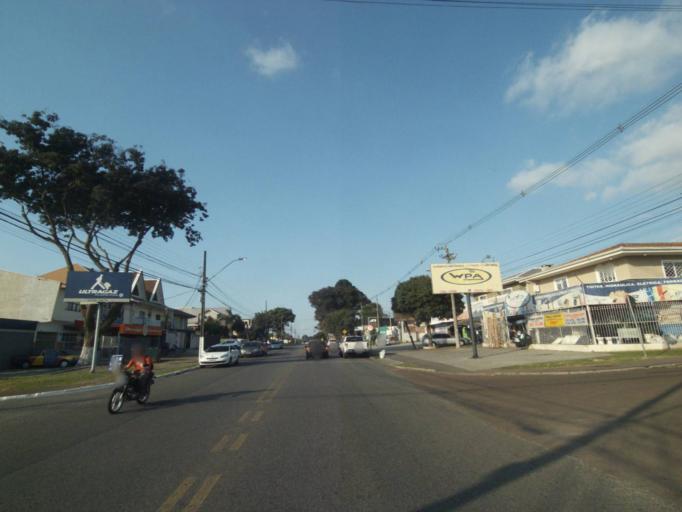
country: BR
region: Parana
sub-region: Curitiba
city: Curitiba
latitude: -25.4836
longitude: -49.3268
